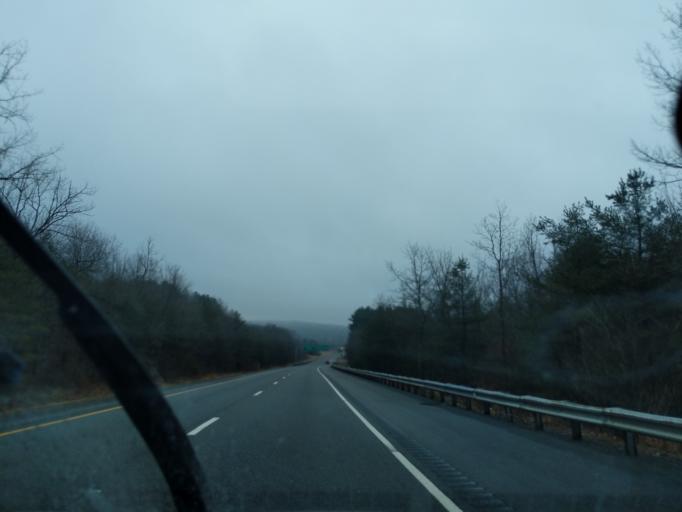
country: US
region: Massachusetts
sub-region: Worcester County
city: Oxford
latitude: 42.1236
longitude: -71.8571
